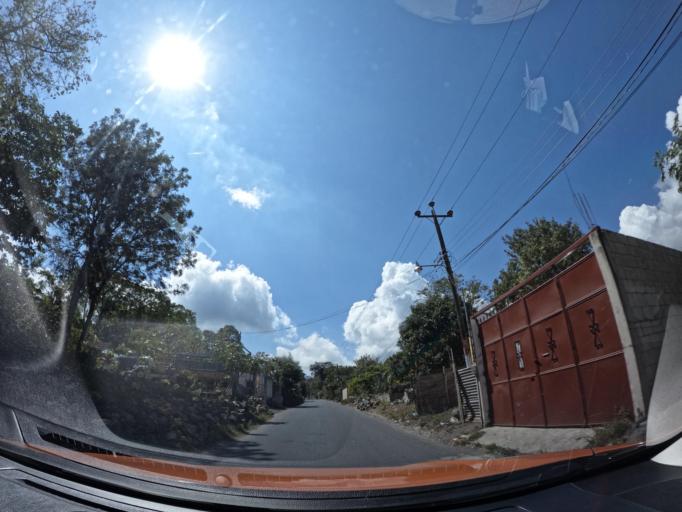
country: GT
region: Solola
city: Santiago Atitlan
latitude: 14.6258
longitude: -91.2333
